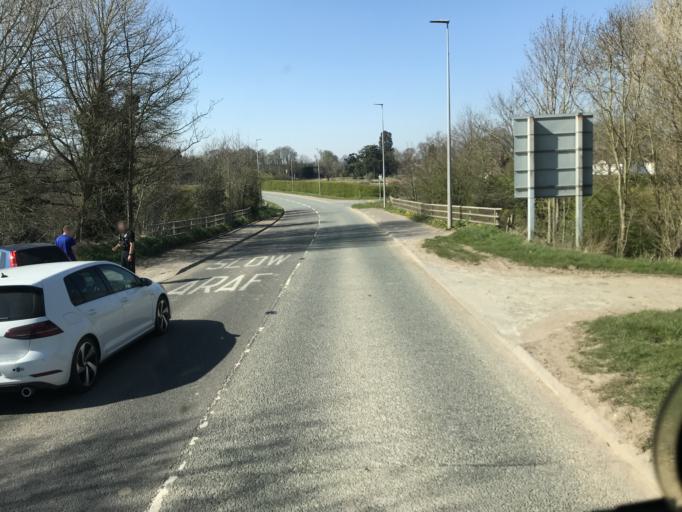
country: GB
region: Wales
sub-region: Wrexham
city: Rossett
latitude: 53.1058
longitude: -2.9595
